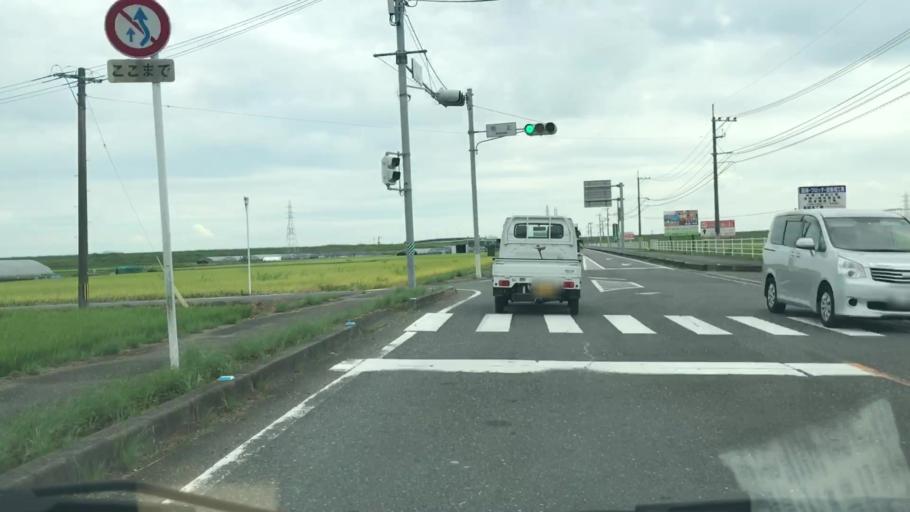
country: JP
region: Saga Prefecture
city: Saga-shi
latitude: 33.2847
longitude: 130.2516
